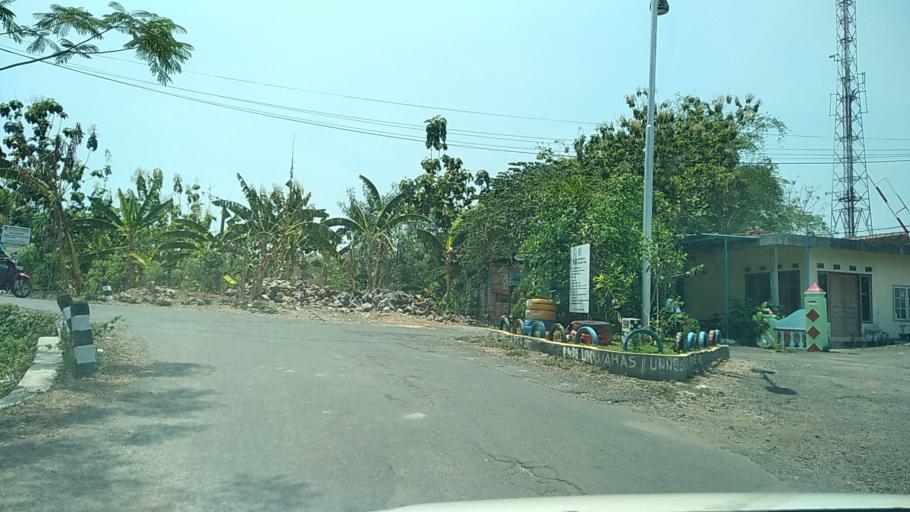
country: ID
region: Central Java
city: Semarang
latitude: -7.0235
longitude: 110.3782
